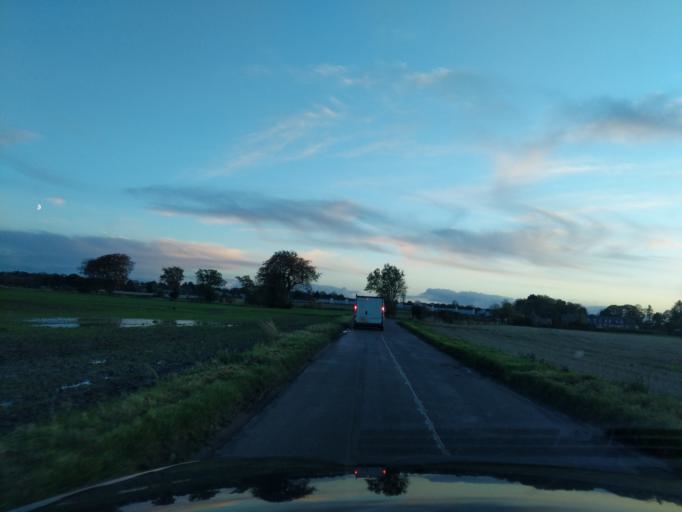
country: GB
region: Scotland
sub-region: Fife
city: Leuchars
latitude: 56.3900
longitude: -2.8749
